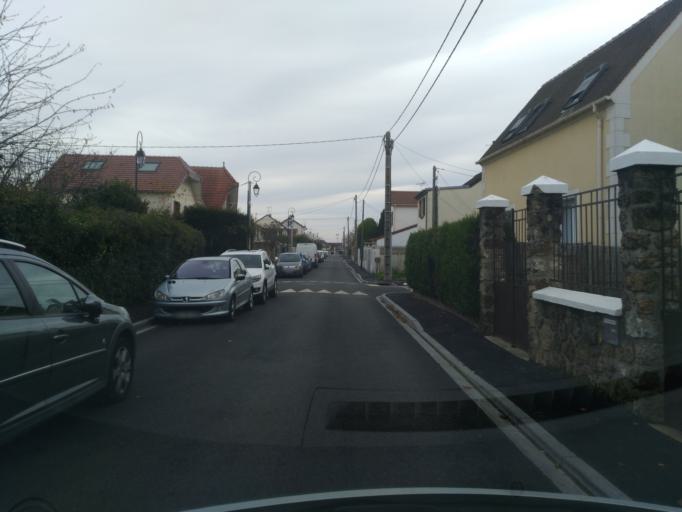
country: FR
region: Ile-de-France
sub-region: Departement des Yvelines
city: Les Clayes-sous-Bois
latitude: 48.8291
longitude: 1.9891
